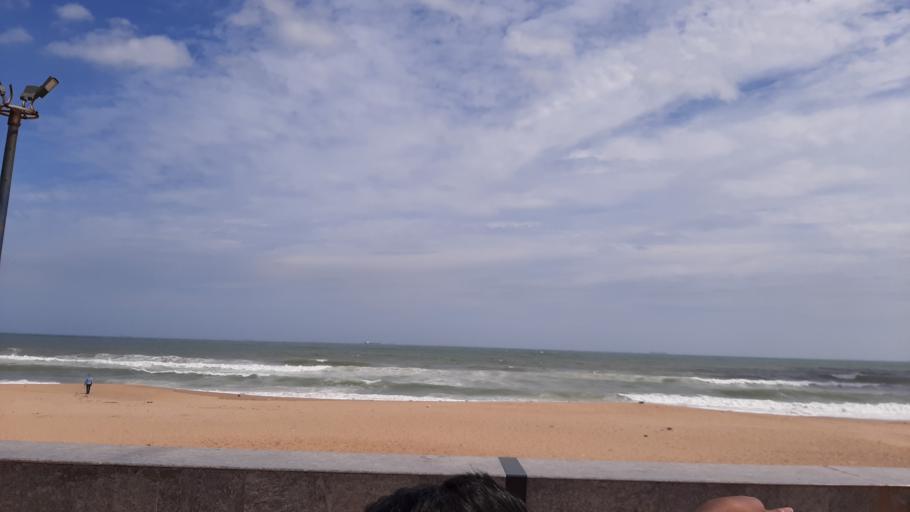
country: IN
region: Andhra Pradesh
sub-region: Vishakhapatnam
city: Yarada
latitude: 17.7184
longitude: 83.3322
